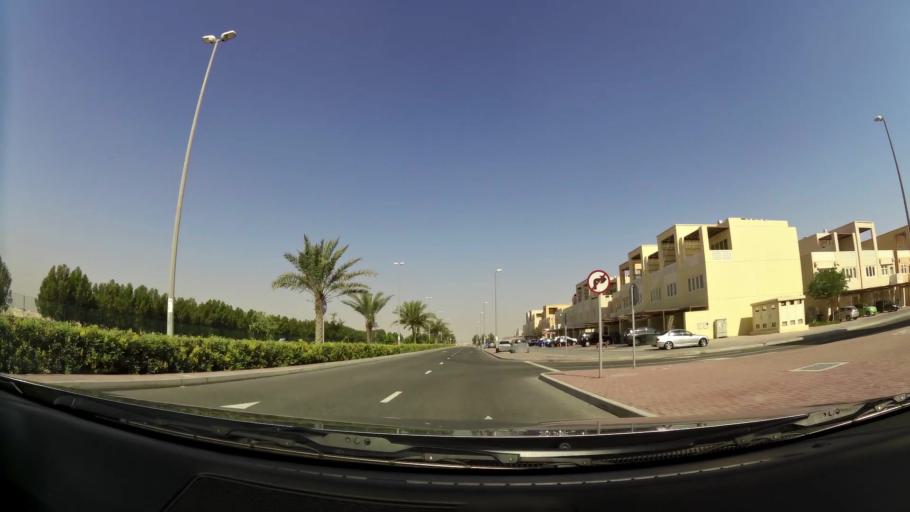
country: AE
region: Dubai
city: Dubai
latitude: 24.9494
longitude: 55.0491
